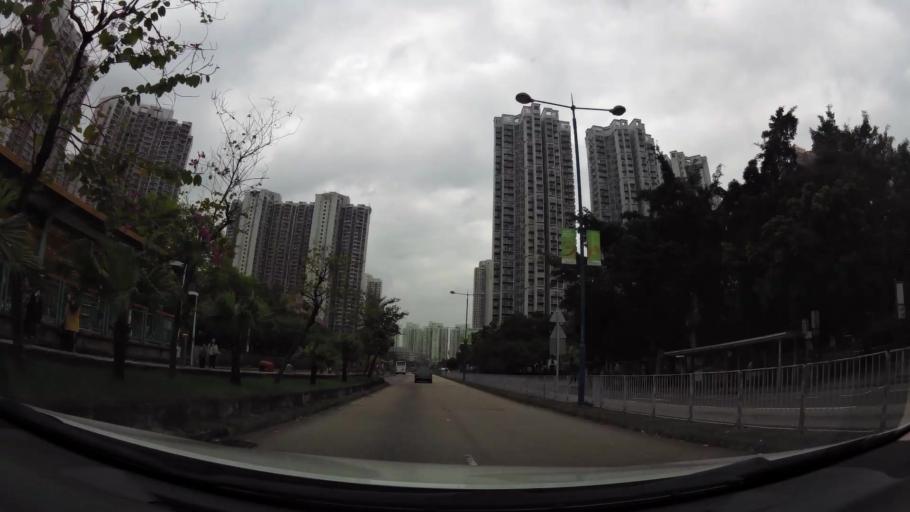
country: HK
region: Yuen Long
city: Yuen Long Kau Hui
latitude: 22.4561
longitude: 113.9995
